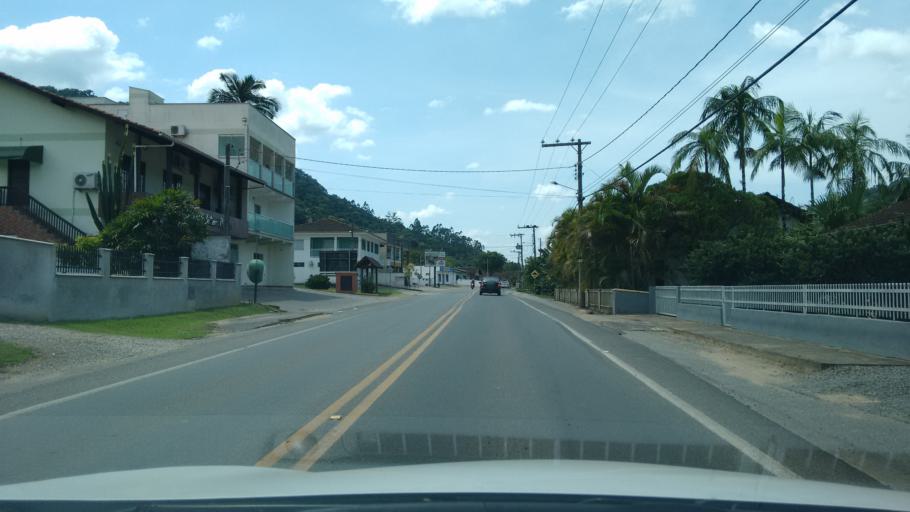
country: BR
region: Santa Catarina
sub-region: Rodeio
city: Gavea
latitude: -26.9031
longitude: -49.3591
